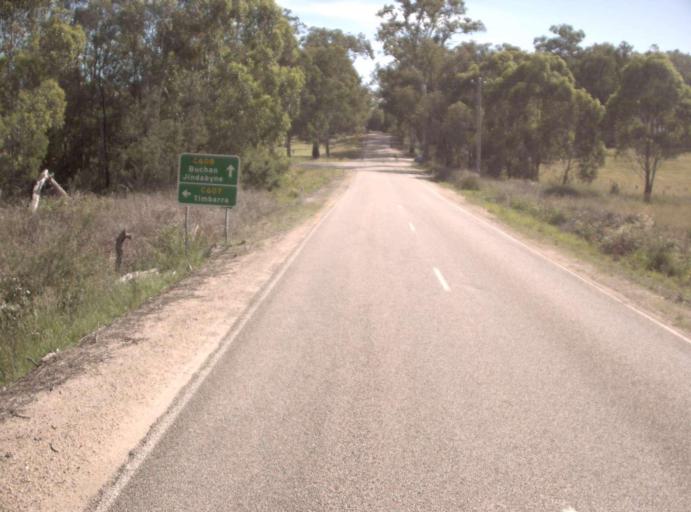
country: AU
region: Victoria
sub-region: East Gippsland
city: Lakes Entrance
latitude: -37.5285
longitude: 148.1557
